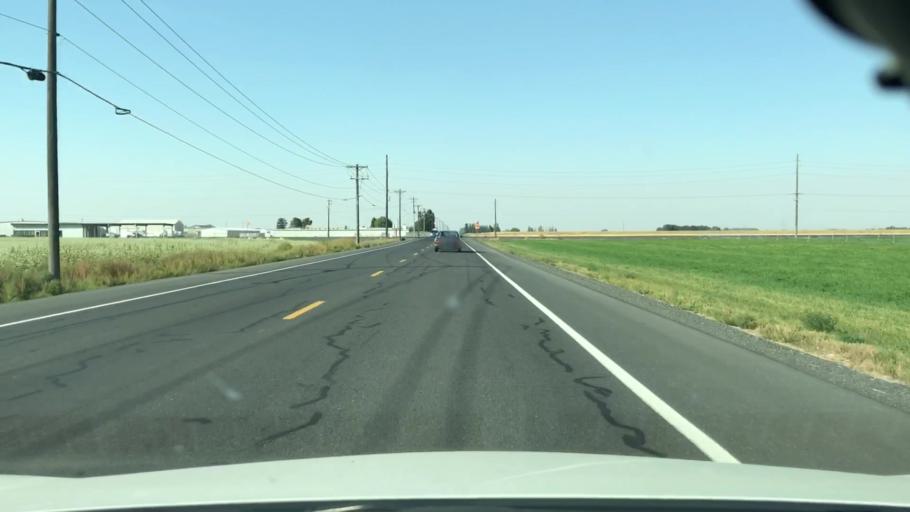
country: US
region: Washington
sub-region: Grant County
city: Moses Lake
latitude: 47.1291
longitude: -119.2358
